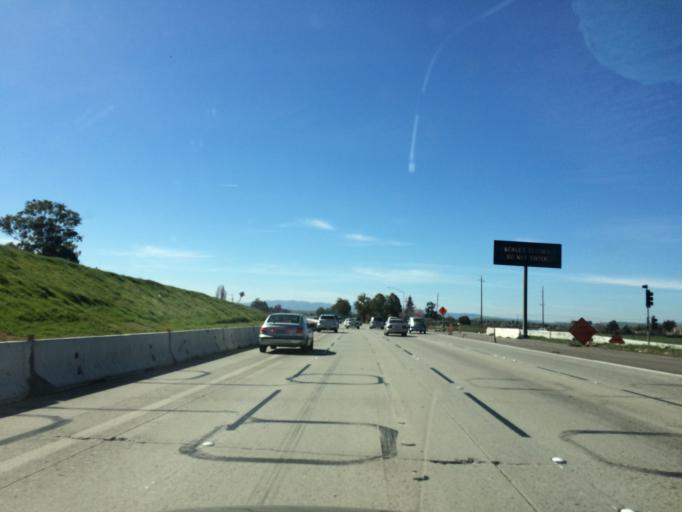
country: US
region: California
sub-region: Alameda County
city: Livermore
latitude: 37.7174
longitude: -121.7043
